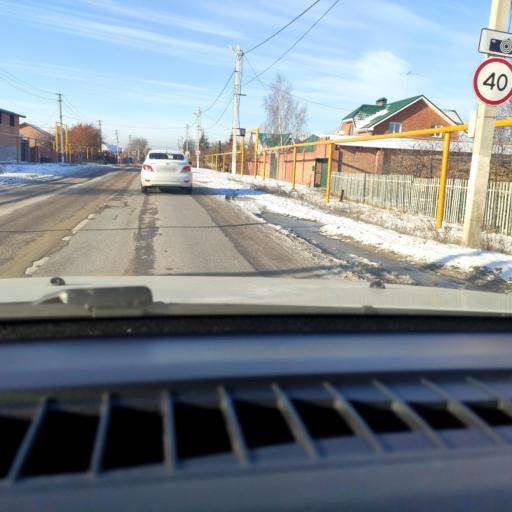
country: RU
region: Samara
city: Podstepki
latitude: 53.5160
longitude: 49.1335
